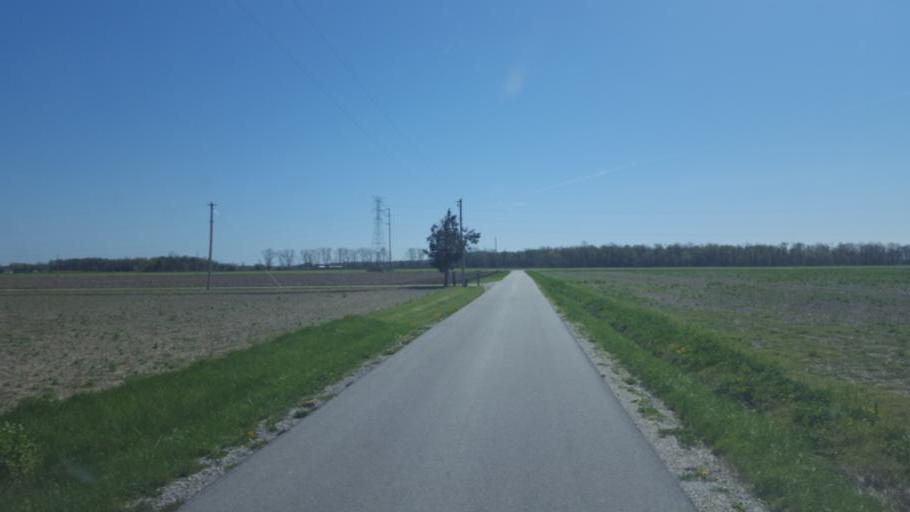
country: US
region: Ohio
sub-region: Ottawa County
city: Oak Harbor
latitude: 41.4504
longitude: -83.1292
